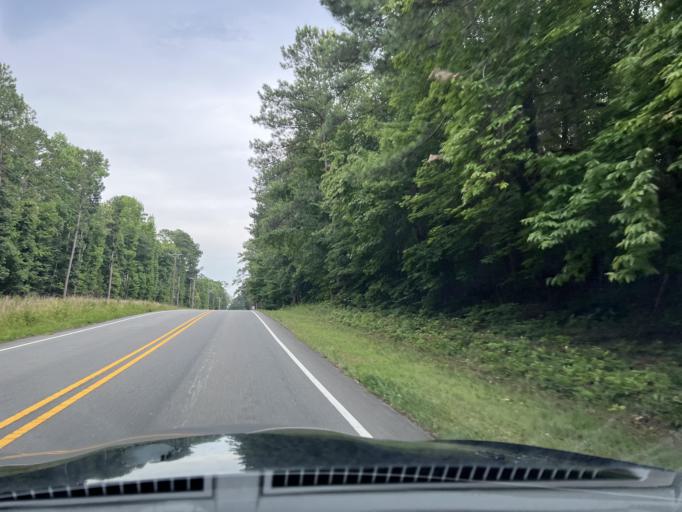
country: US
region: North Carolina
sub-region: Wake County
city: Wake Forest
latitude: 36.0147
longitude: -78.5693
